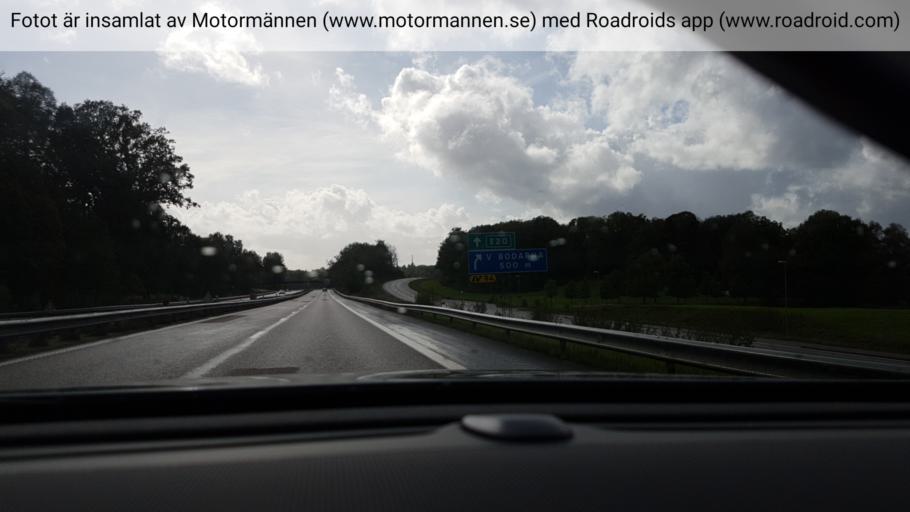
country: SE
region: Vaestra Goetaland
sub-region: Alingsas Kommun
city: Alingsas
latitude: 57.9015
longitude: 12.4953
